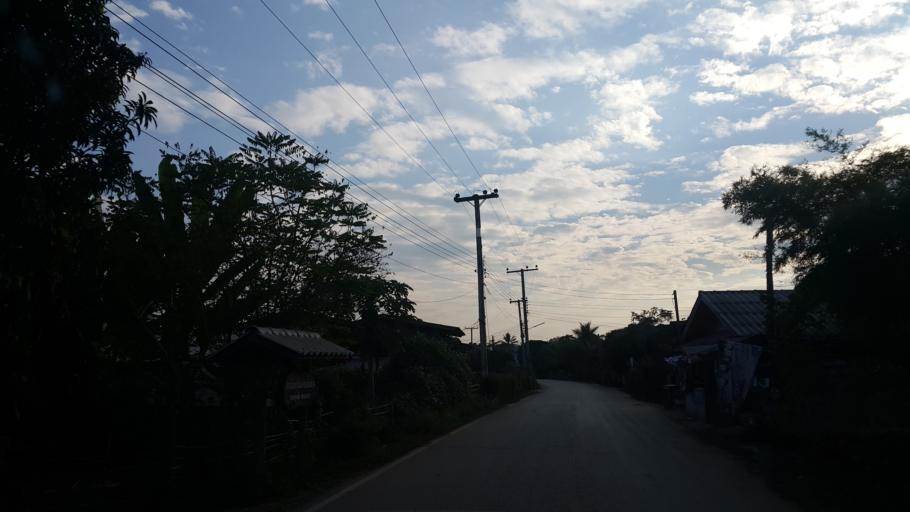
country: TH
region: Lampang
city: Sop Prap
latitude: 17.9044
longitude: 99.3296
